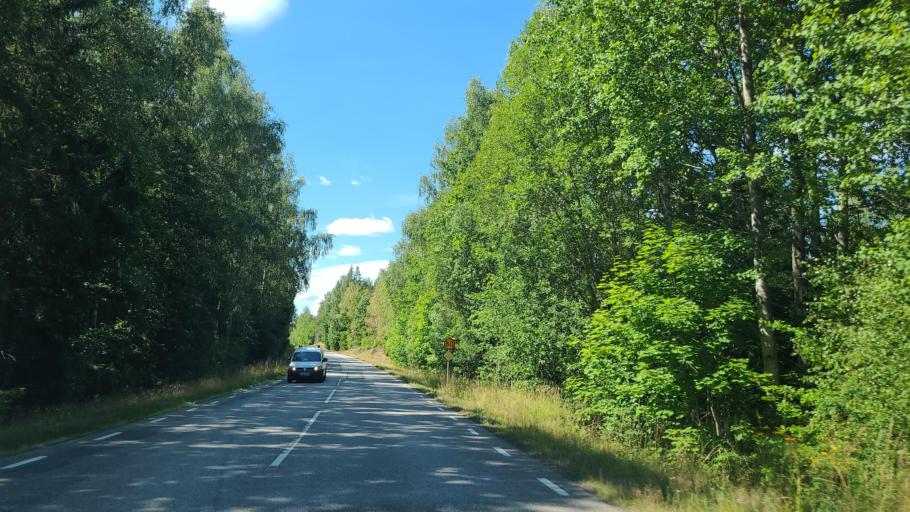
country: SE
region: Kalmar
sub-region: Emmaboda Kommun
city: Emmaboda
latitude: 56.5495
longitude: 15.6975
